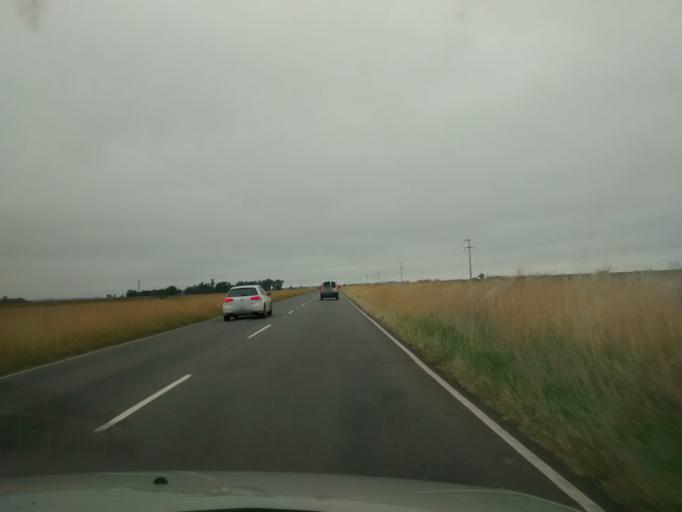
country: AR
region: Buenos Aires
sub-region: Partido de Ayacucho
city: Ayacucho
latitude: -37.0457
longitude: -58.5415
